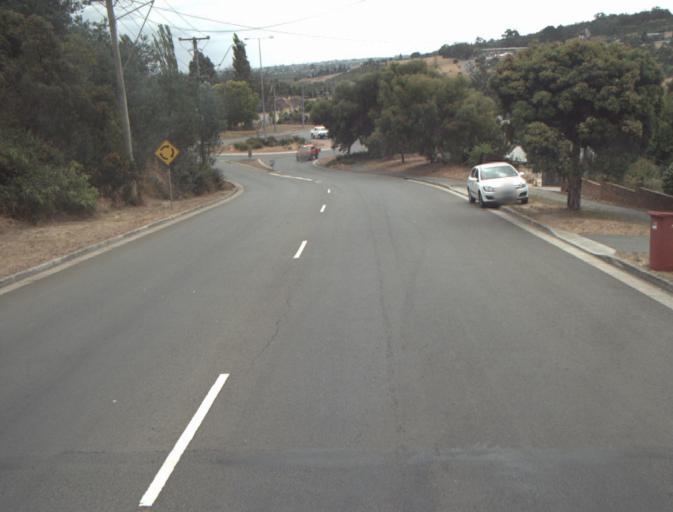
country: AU
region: Tasmania
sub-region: Launceston
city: Newstead
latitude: -41.4386
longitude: 147.1780
